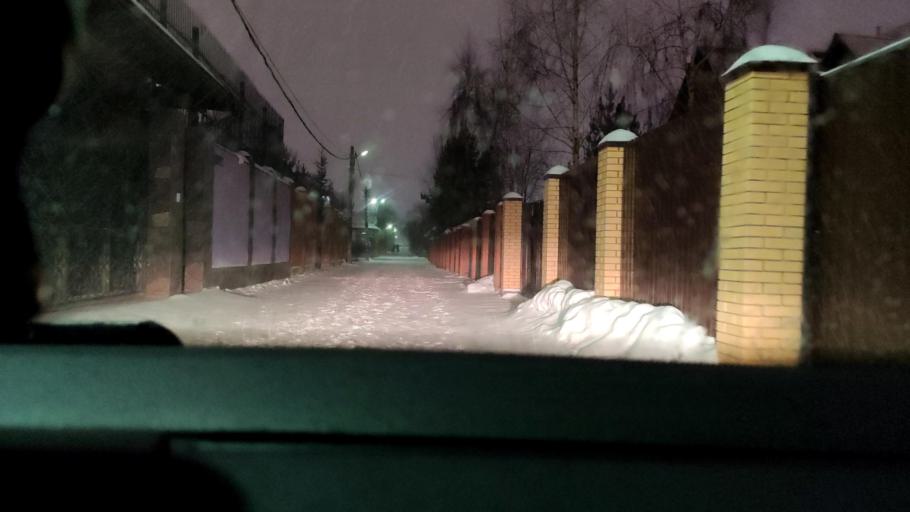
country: RU
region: Moskovskaya
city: Mosrentgen
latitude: 55.6283
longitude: 37.4624
